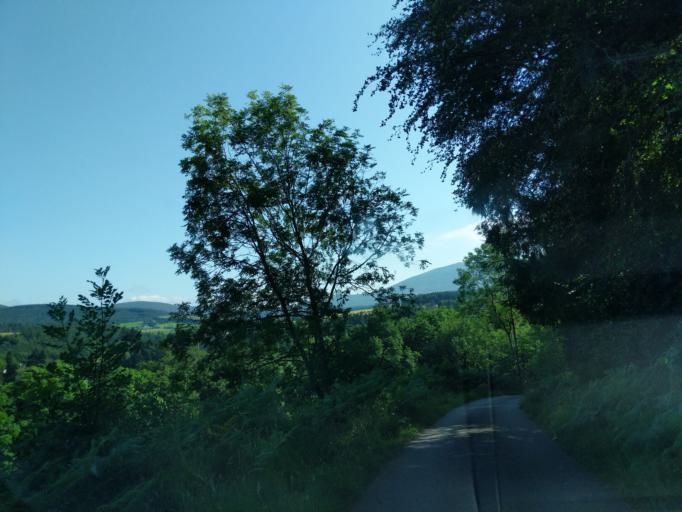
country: GB
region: Scotland
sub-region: Moray
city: Rothes
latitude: 57.4706
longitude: -3.2357
